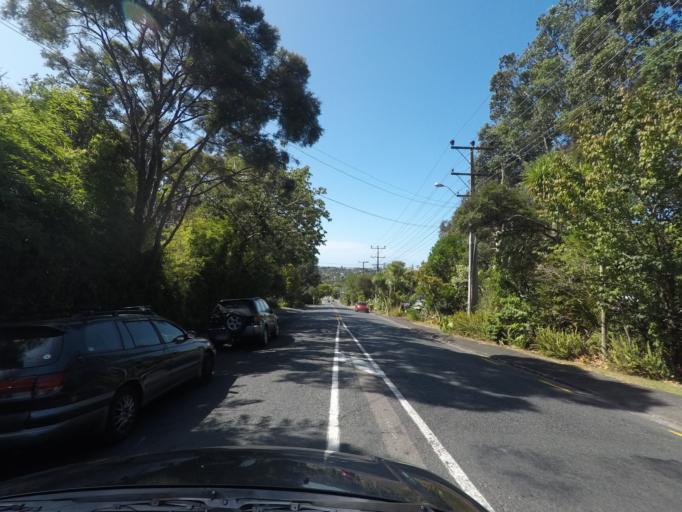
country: NZ
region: Auckland
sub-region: Auckland
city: Titirangi
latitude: -36.9347
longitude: 174.6549
